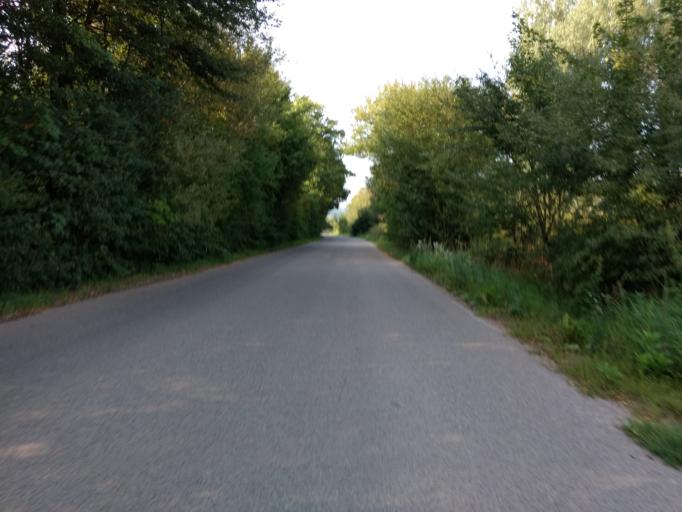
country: DE
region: Saarland
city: Rehlingen-Siersburg
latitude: 49.3701
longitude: 6.7011
